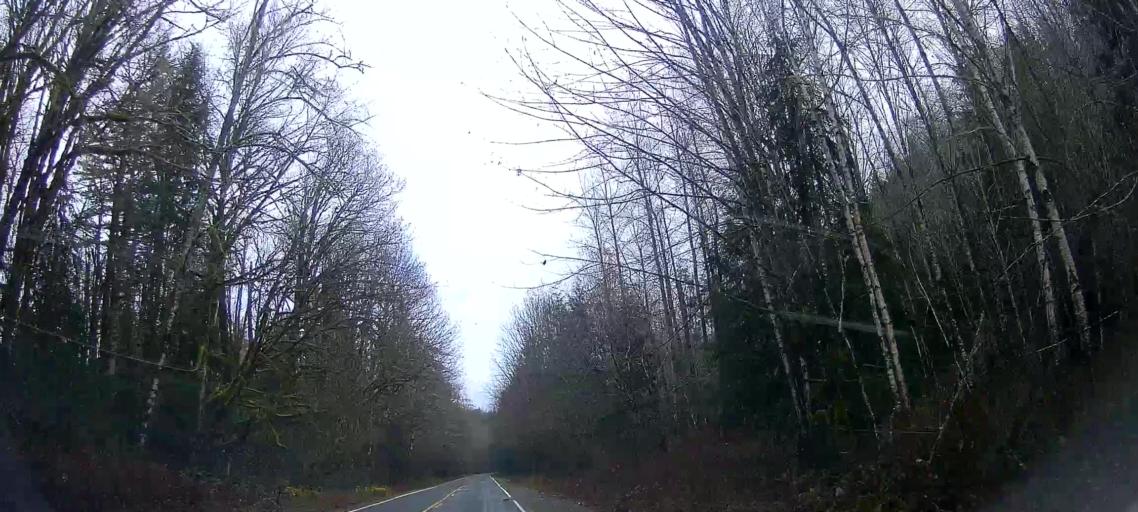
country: US
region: Washington
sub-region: Snohomish County
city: Darrington
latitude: 48.4864
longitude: -121.4852
